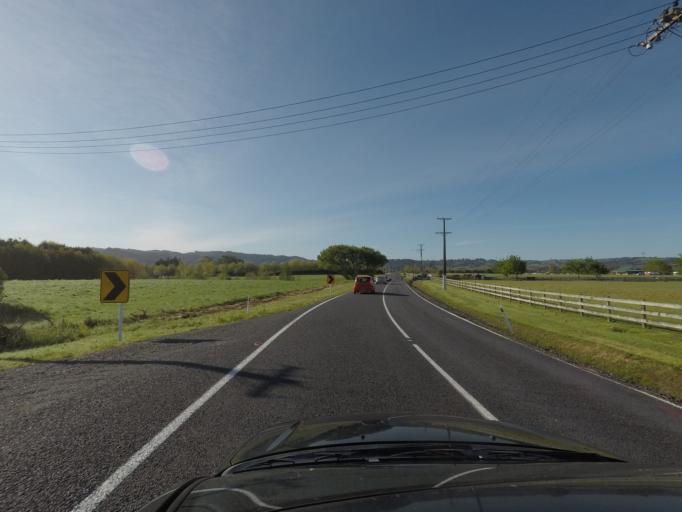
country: NZ
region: Auckland
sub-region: Auckland
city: Red Hill
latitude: -37.0031
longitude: 175.0431
